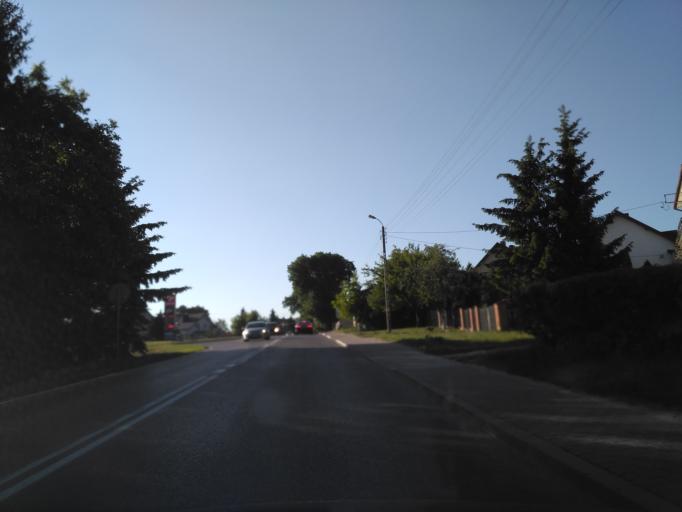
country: PL
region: Lublin Voivodeship
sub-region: Powiat lubelski
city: Bychawa
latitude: 51.0179
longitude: 22.5247
